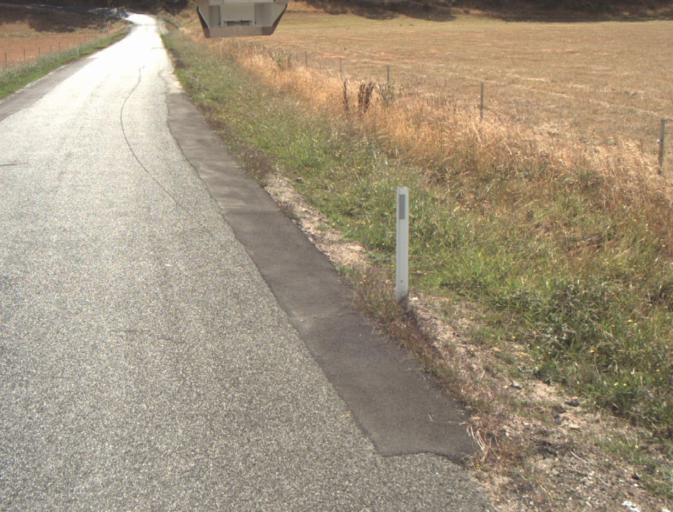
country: AU
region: Tasmania
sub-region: Launceston
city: Mayfield
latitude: -41.2469
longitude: 147.1492
